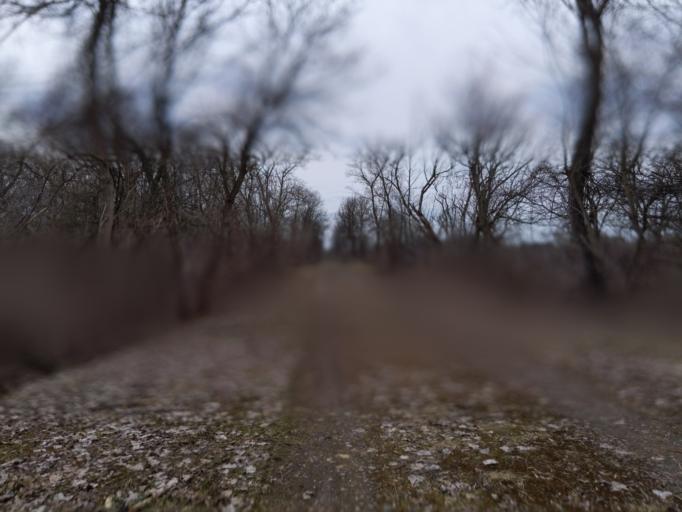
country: US
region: New York
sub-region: Tompkins County
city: Dryden
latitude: 42.4965
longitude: -76.3150
